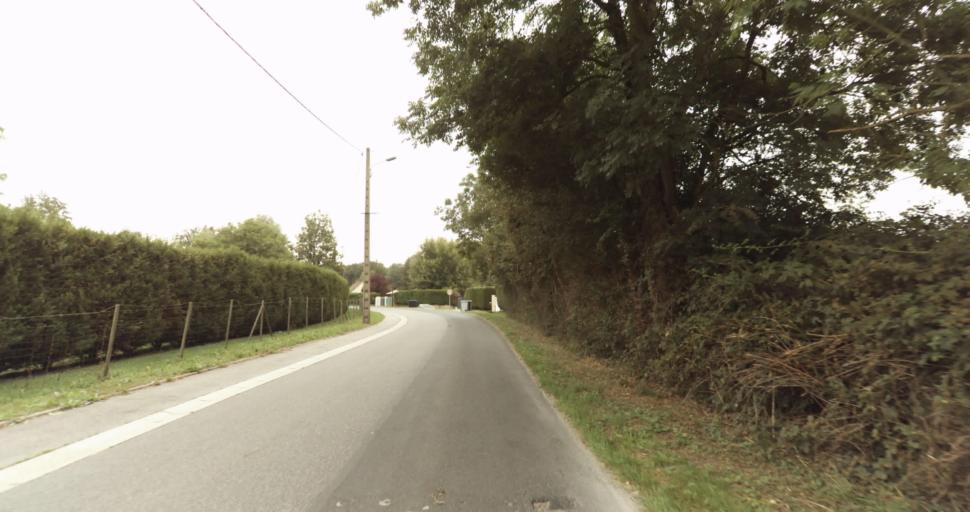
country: FR
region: Haute-Normandie
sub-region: Departement de l'Eure
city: Marcilly-sur-Eure
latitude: 48.8232
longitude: 1.3497
